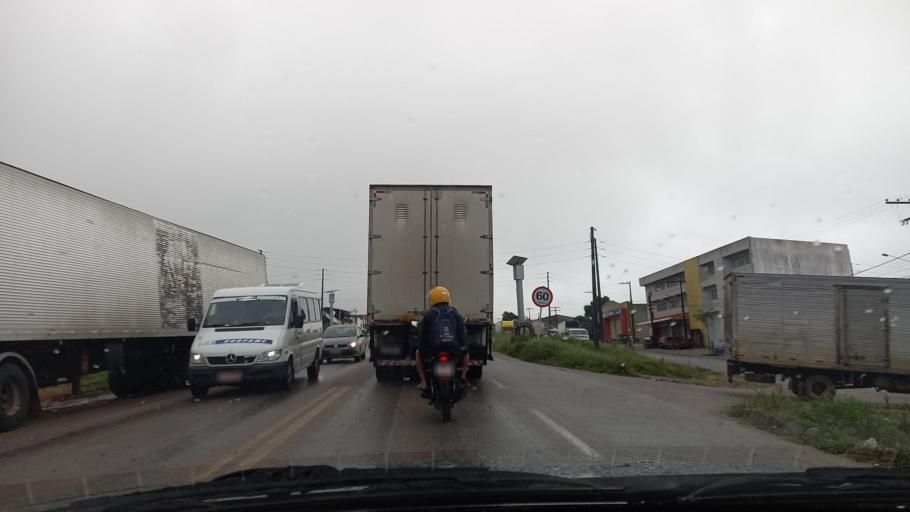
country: BR
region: Pernambuco
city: Garanhuns
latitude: -8.8813
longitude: -36.4910
